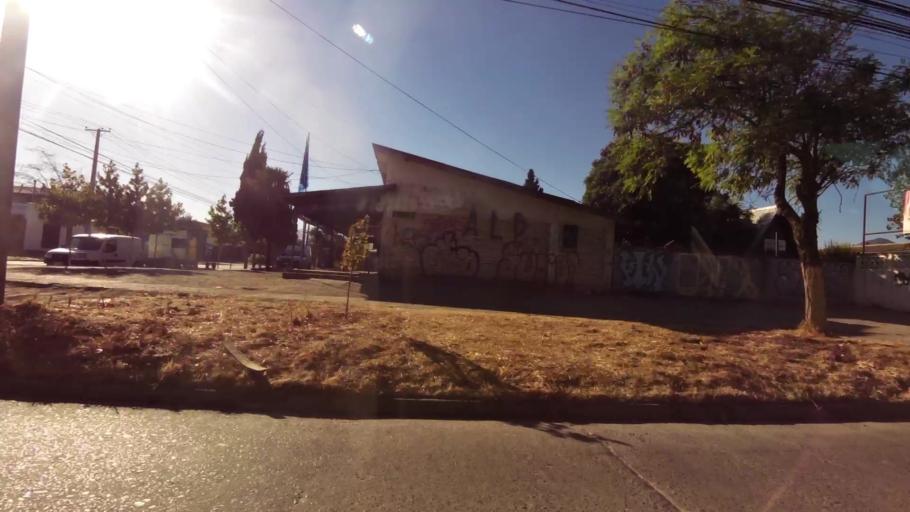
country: CL
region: O'Higgins
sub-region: Provincia de Cachapoal
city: Rancagua
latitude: -34.1769
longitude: -70.7234
